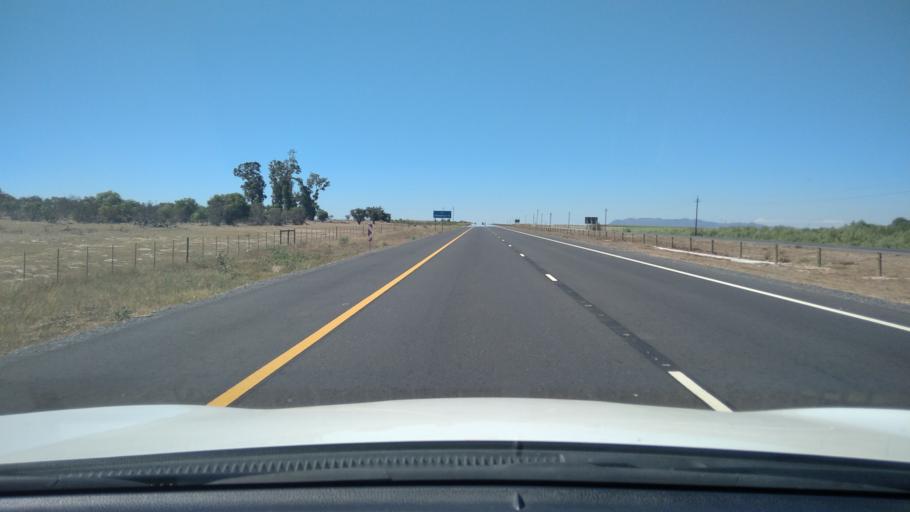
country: ZA
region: Western Cape
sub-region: West Coast District Municipality
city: Malmesbury
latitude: -33.5596
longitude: 18.6266
